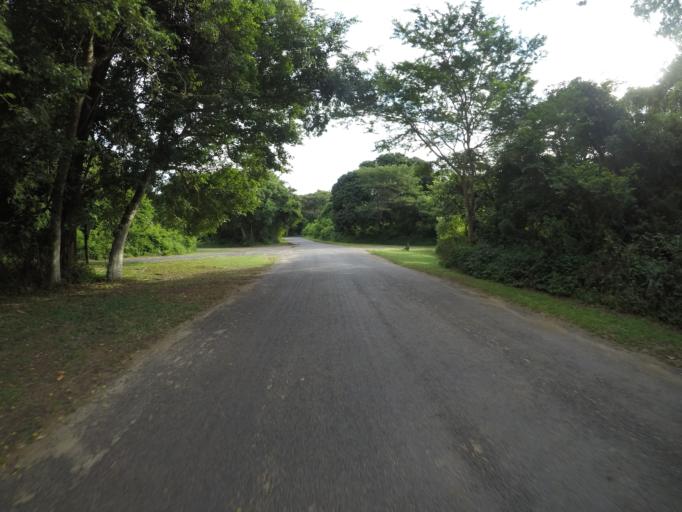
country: ZA
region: KwaZulu-Natal
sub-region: uMkhanyakude District Municipality
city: Mtubatuba
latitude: -28.3849
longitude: 32.4106
